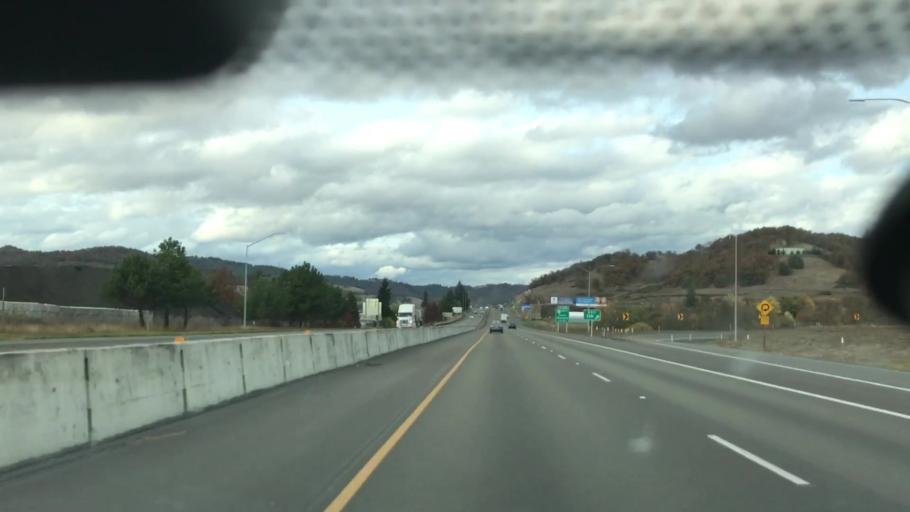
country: US
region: Oregon
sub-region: Douglas County
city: Green
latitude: 43.1550
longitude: -123.3653
